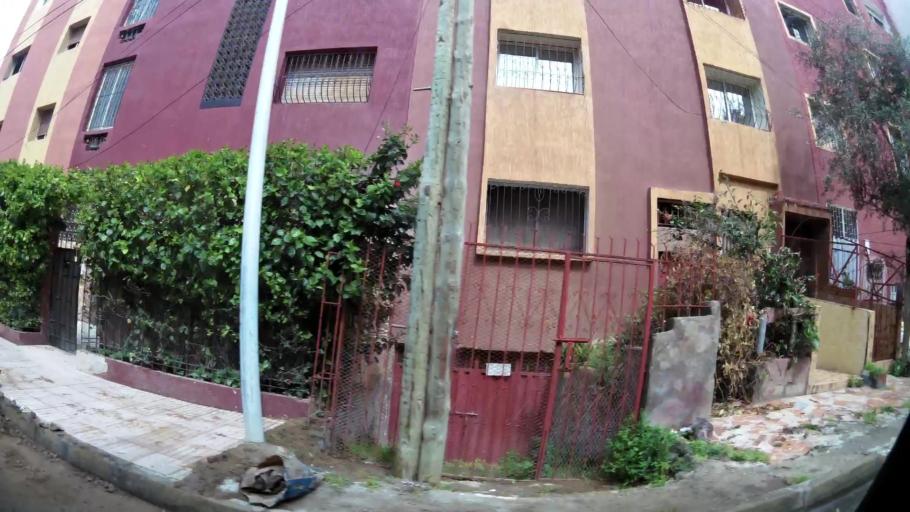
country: MA
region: Grand Casablanca
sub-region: Casablanca
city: Casablanca
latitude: 33.5679
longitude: -7.6951
